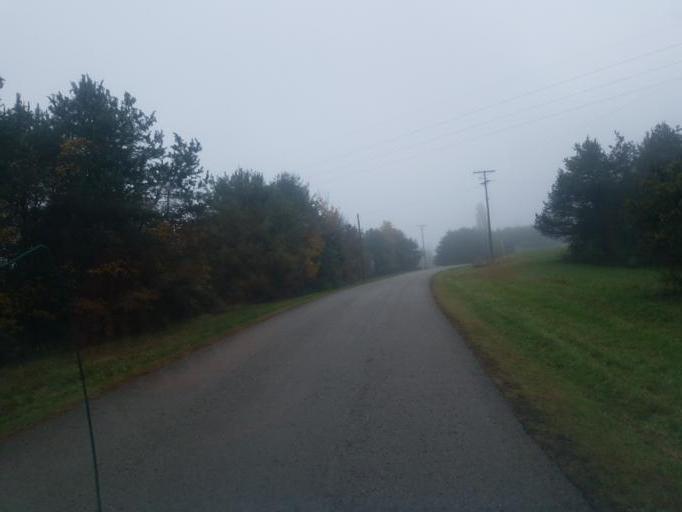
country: US
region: Ohio
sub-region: Morgan County
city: McConnelsville
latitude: 39.5223
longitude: -81.7945
